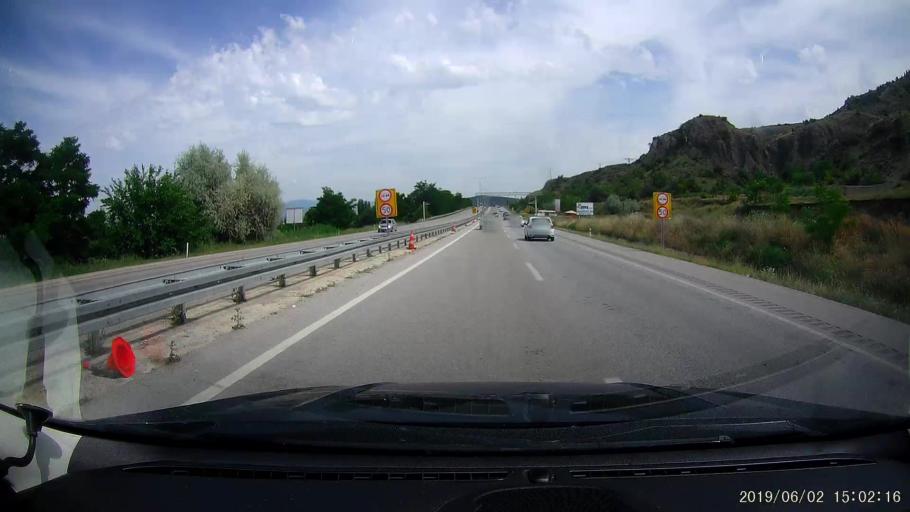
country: TR
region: Corum
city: Osmancik
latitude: 40.9827
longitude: 34.7643
